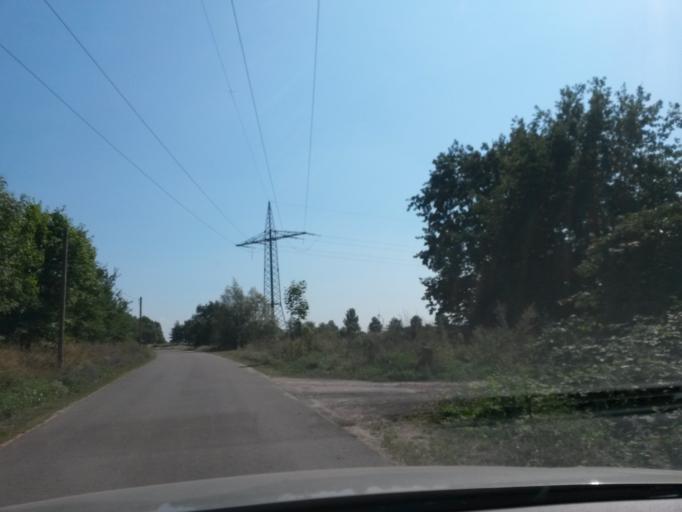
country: DE
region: Saxony-Anhalt
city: Jerichow
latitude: 52.3916
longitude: 11.9902
